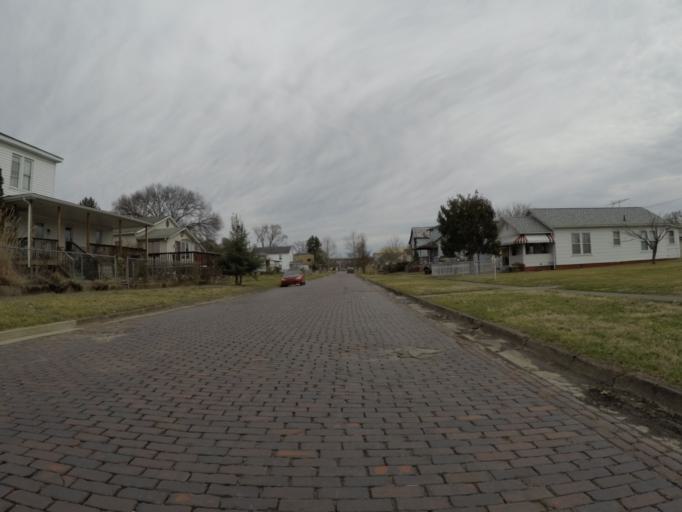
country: US
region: West Virginia
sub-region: Cabell County
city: Huntington
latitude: 38.4083
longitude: -82.4865
